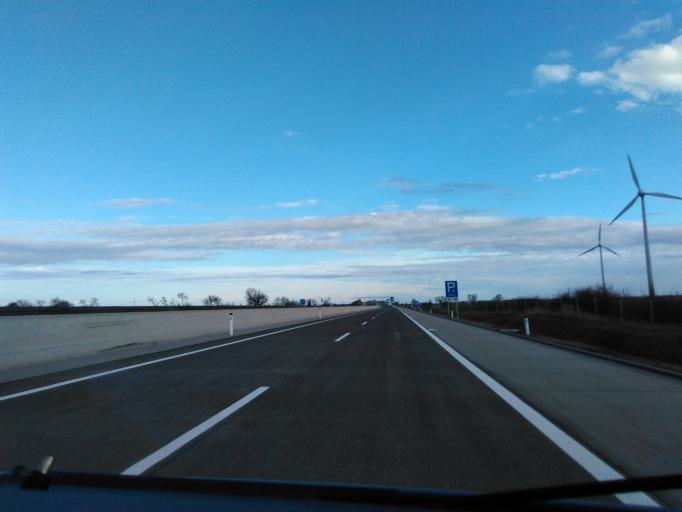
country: AT
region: Burgenland
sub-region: Politischer Bezirk Neusiedl am See
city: Kittsee
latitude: 48.0779
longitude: 17.0525
